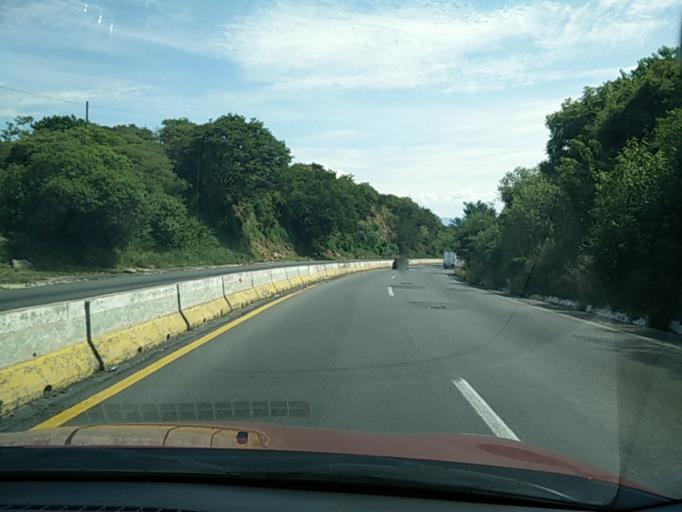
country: MX
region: Jalisco
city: Ixtlahuacan de los Membrillos
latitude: 20.3328
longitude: -103.1840
